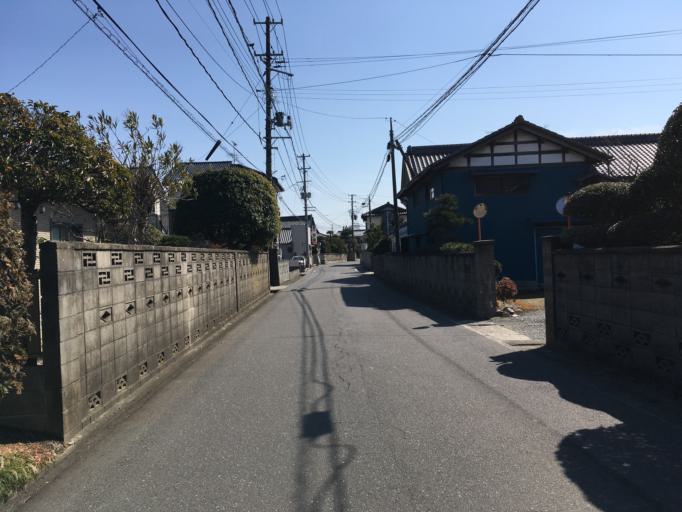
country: JP
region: Fukushima
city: Iwaki
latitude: 36.9423
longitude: 140.8616
